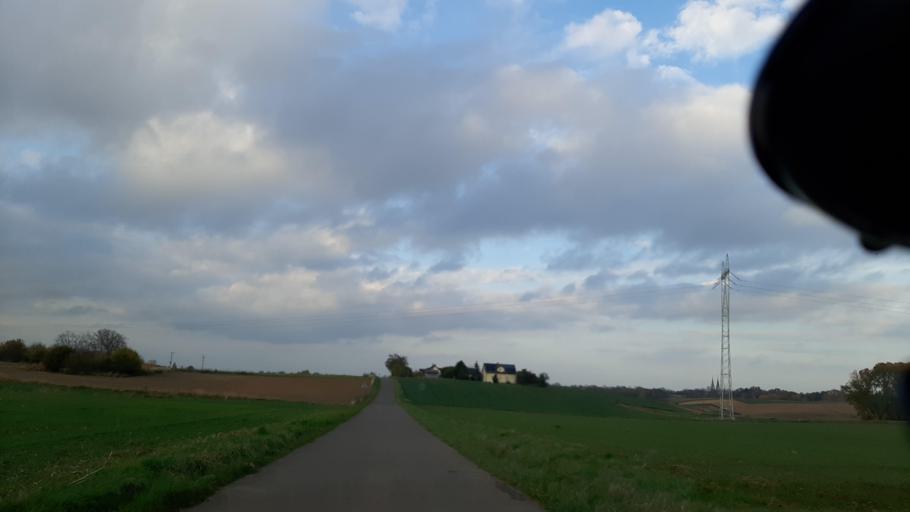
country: PL
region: Lublin Voivodeship
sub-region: Powiat lubelski
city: Garbow
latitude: 51.3379
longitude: 22.3246
